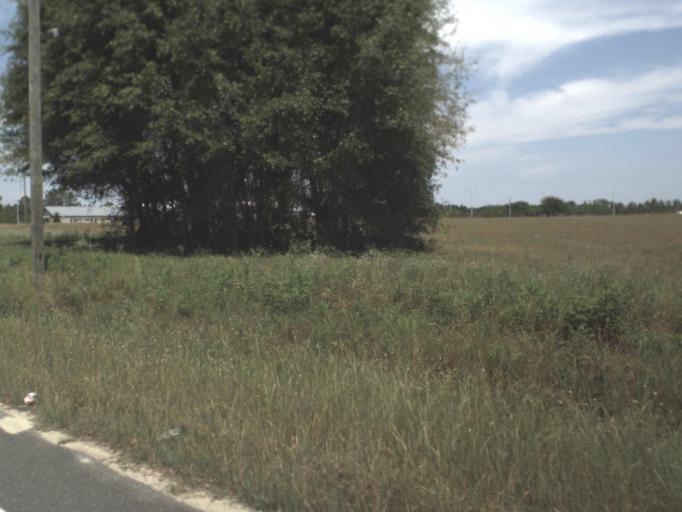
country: US
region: Florida
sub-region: Jackson County
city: Marianna
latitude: 30.8122
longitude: -85.1769
